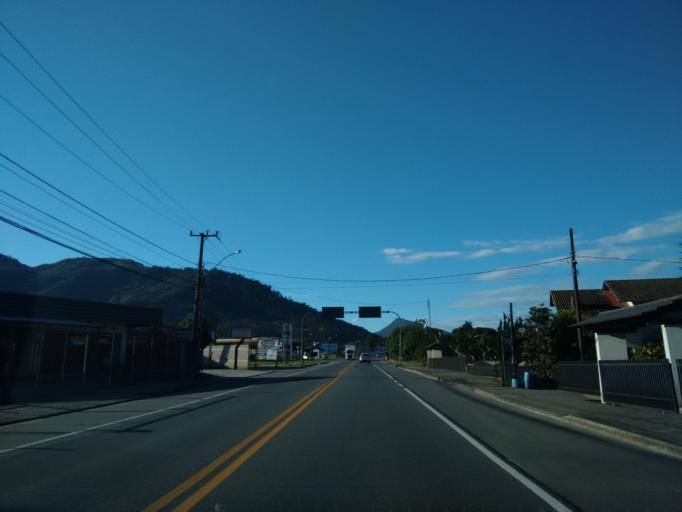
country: BR
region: Santa Catarina
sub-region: Pomerode
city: Pomerode
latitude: -26.7561
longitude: -49.1723
